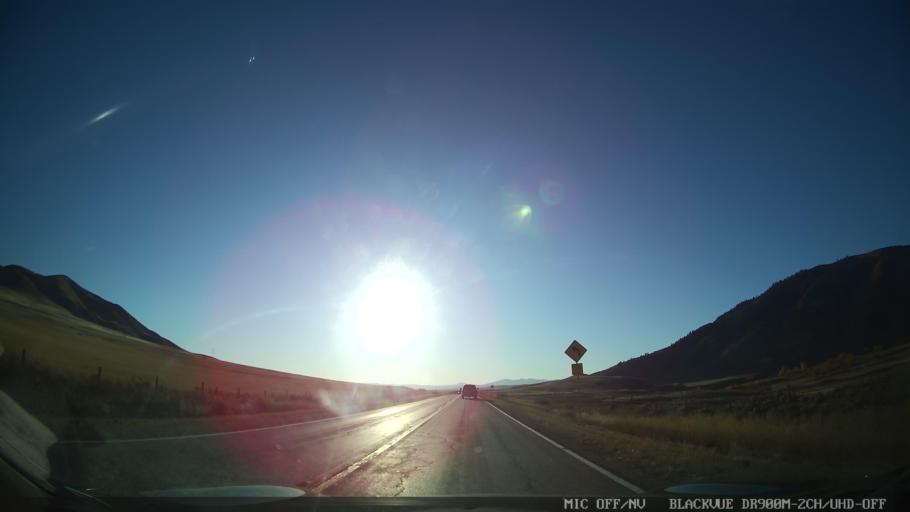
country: US
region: Colorado
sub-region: Grand County
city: Kremmling
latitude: 40.0516
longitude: -106.3552
